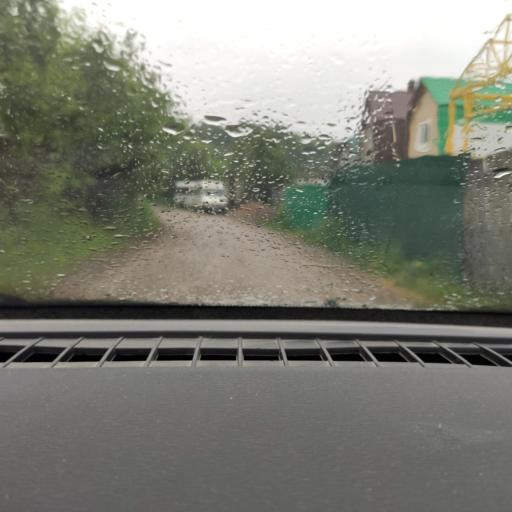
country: RU
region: Perm
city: Perm
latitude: 58.0323
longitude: 56.3512
